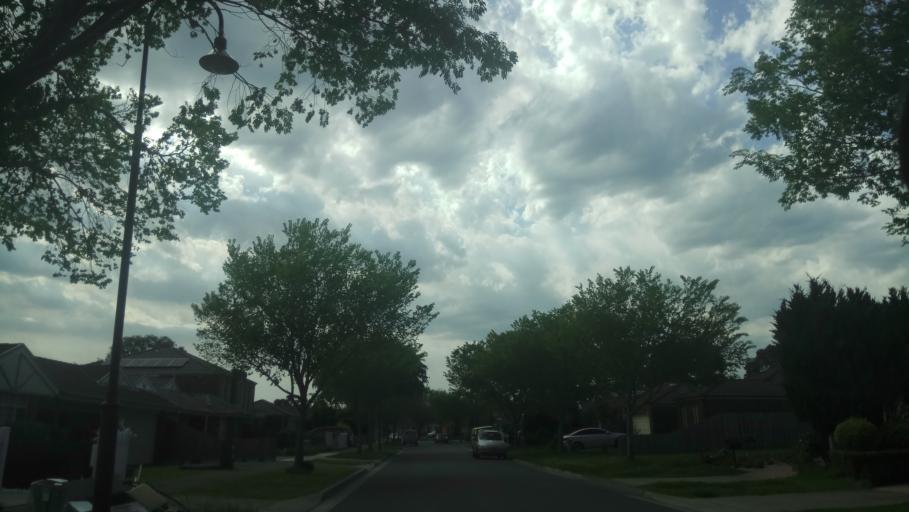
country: AU
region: Victoria
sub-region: Casey
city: Lynbrook
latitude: -38.0500
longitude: 145.2492
